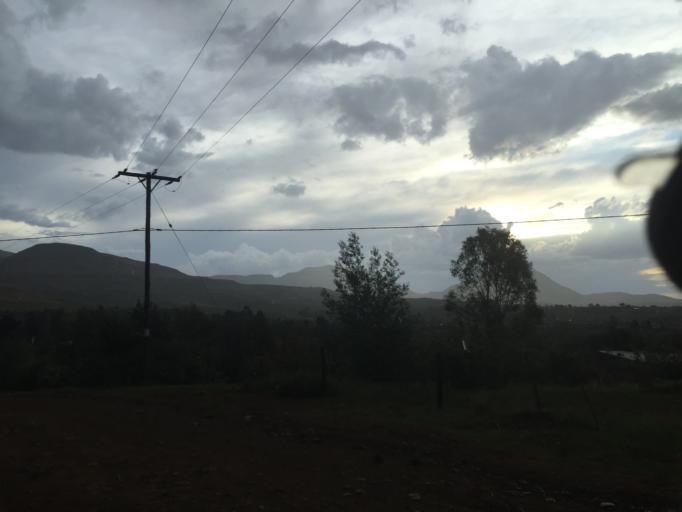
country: LS
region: Berea
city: Teyateyaneng
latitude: -29.1589
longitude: 28.0333
